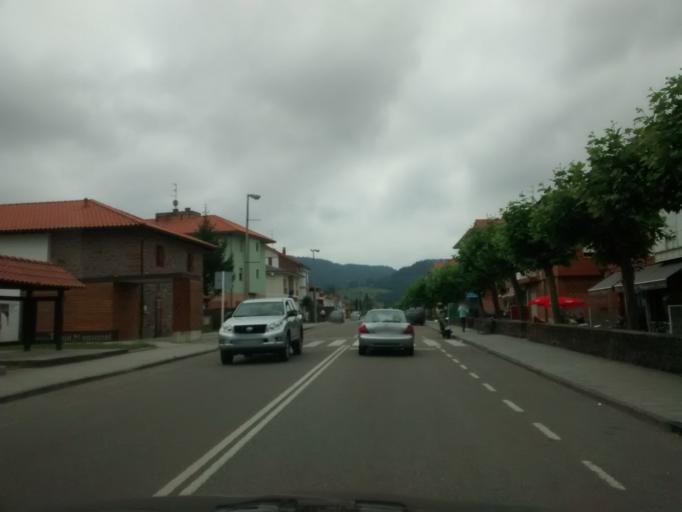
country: ES
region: Cantabria
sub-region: Provincia de Cantabria
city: Cabezon de la Sal
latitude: 43.3022
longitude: -4.2378
